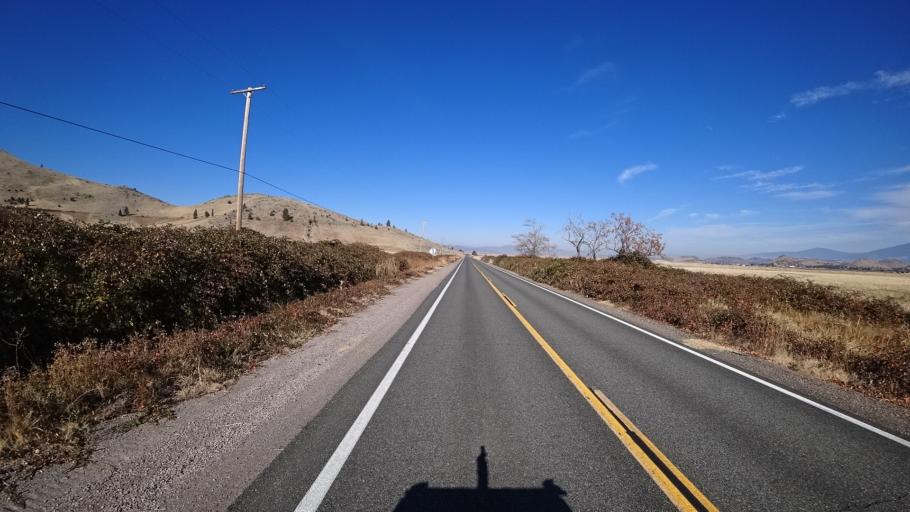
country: US
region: California
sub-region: Siskiyou County
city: Weed
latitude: 41.4597
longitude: -122.4624
